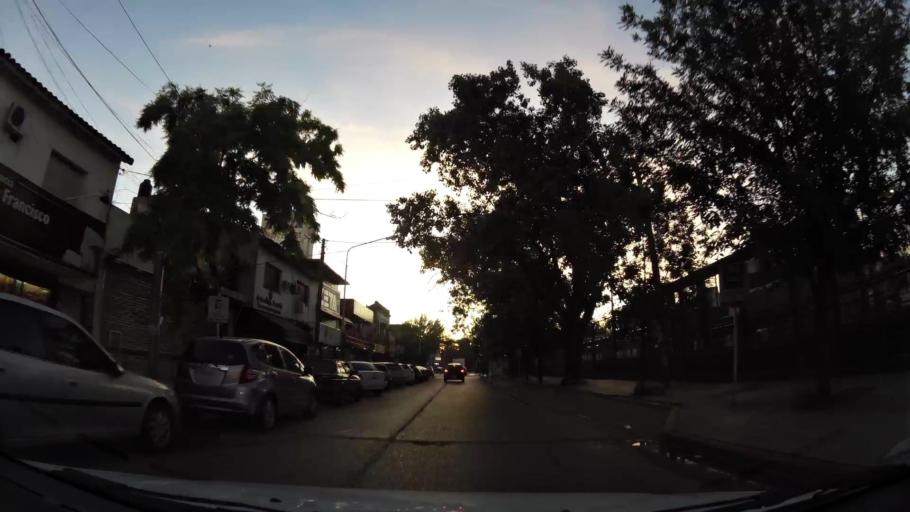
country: AR
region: Buenos Aires
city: Ituzaingo
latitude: -34.6520
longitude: -58.6410
